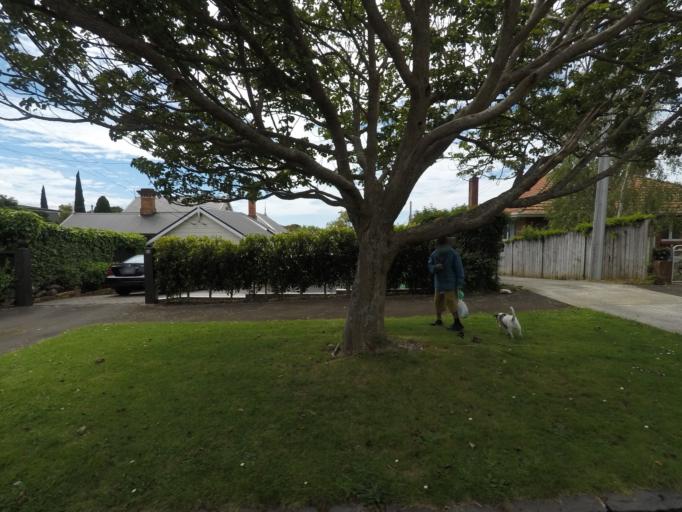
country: NZ
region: Auckland
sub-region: Auckland
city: Auckland
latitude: -36.8844
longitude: 174.7198
